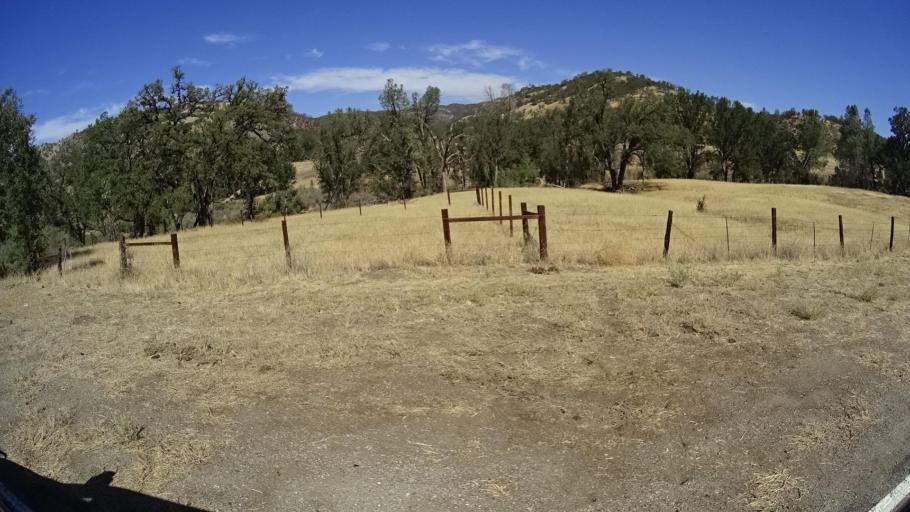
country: US
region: California
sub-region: Fresno County
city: Coalinga
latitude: 36.2011
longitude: -120.7290
